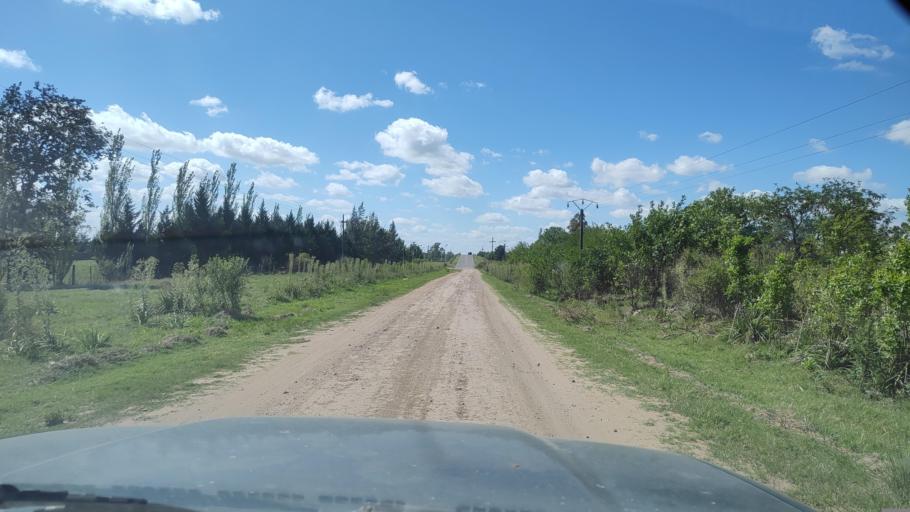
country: AR
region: Buenos Aires
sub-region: Partido de Lujan
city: Lujan
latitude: -34.5394
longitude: -59.1443
